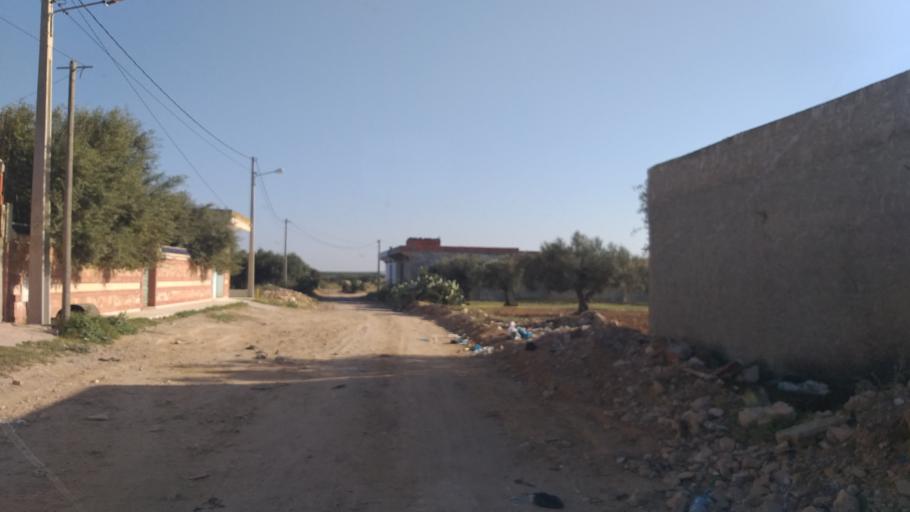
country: TN
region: Al Mahdiyah
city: El Jem
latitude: 35.2823
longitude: 10.7110
